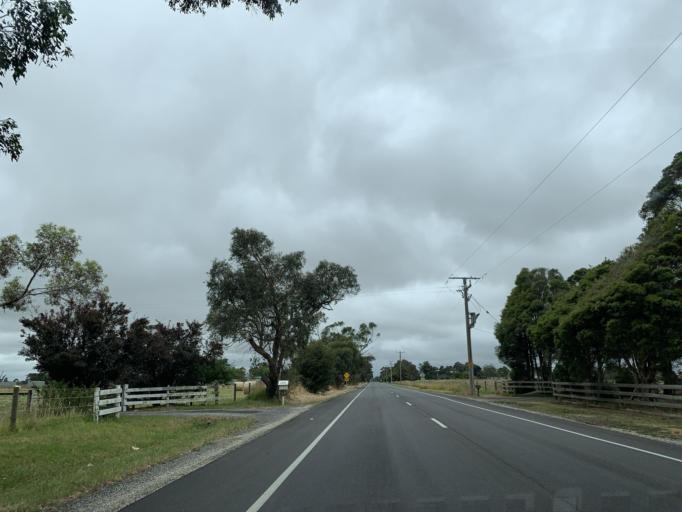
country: AU
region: Victoria
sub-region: Cardinia
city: Officer South
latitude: -38.1416
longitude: 145.3890
